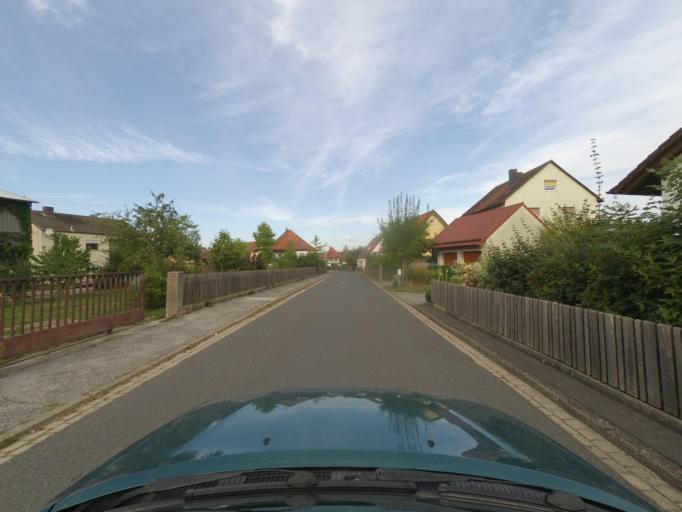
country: DE
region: Bavaria
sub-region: Upper Palatinate
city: Pyrbaum
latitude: 49.2965
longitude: 11.2878
